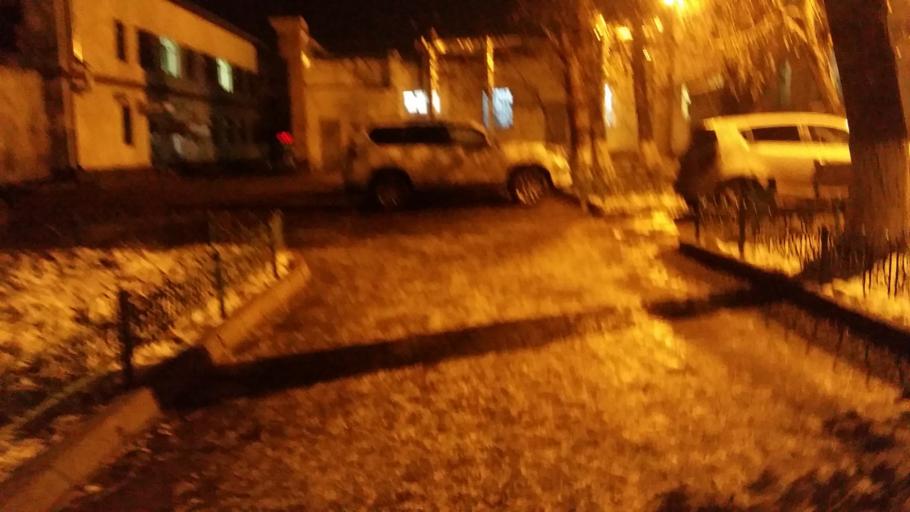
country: KZ
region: Astana Qalasy
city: Astana
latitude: 51.1539
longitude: 71.4848
